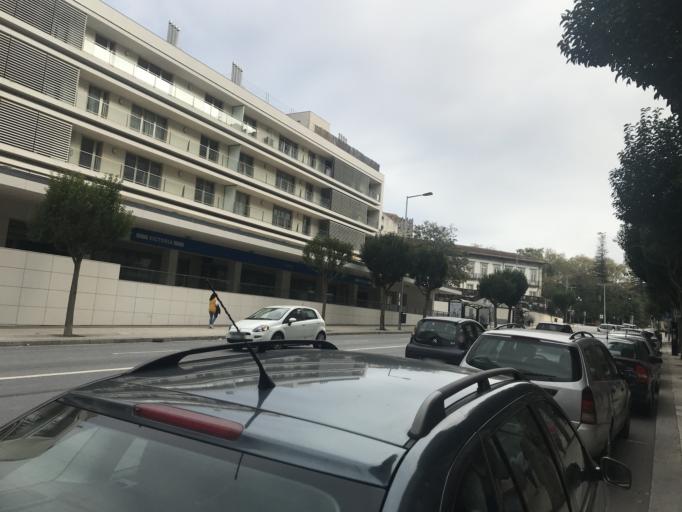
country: PT
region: Porto
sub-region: Porto
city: Porto
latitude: 41.1500
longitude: -8.6258
